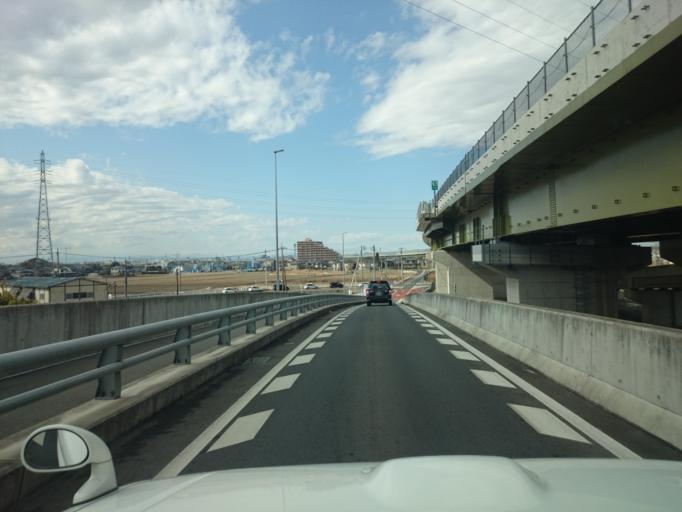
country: JP
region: Saitama
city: Satte
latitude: 36.0632
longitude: 139.7137
